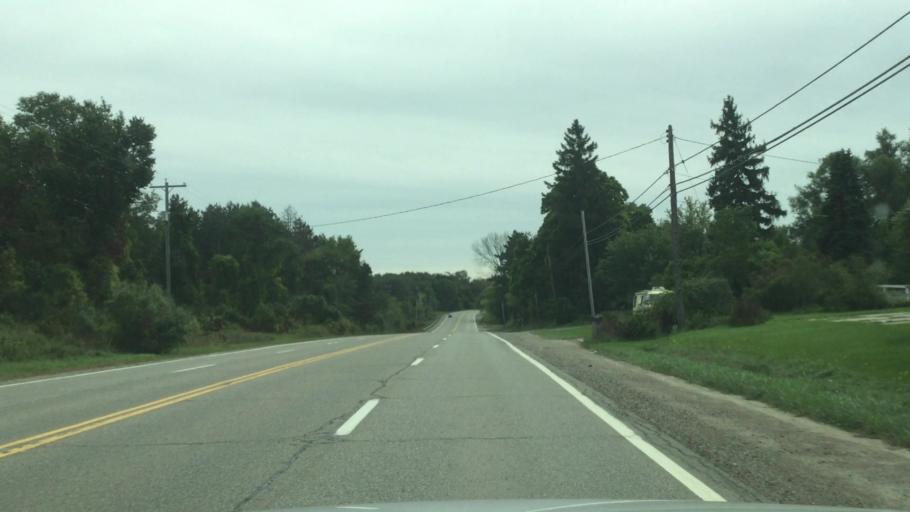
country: US
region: Michigan
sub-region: Oakland County
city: Holly
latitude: 42.8129
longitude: -83.5428
